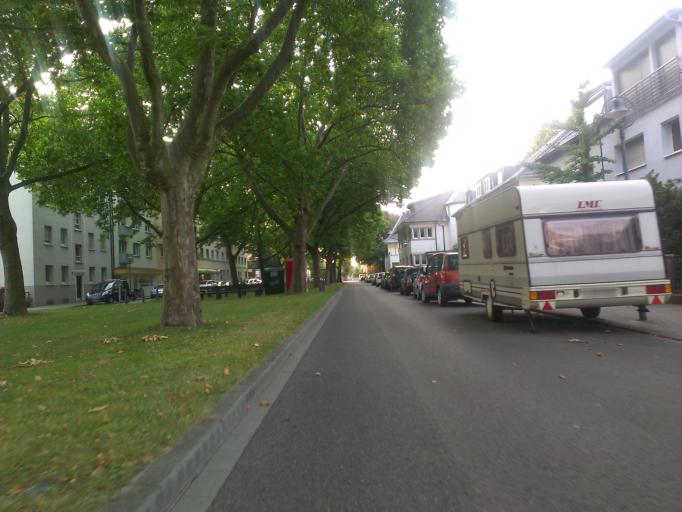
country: DE
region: Rheinland-Pfalz
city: Ludwigshafen am Rhein
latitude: 49.4685
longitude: 8.4577
